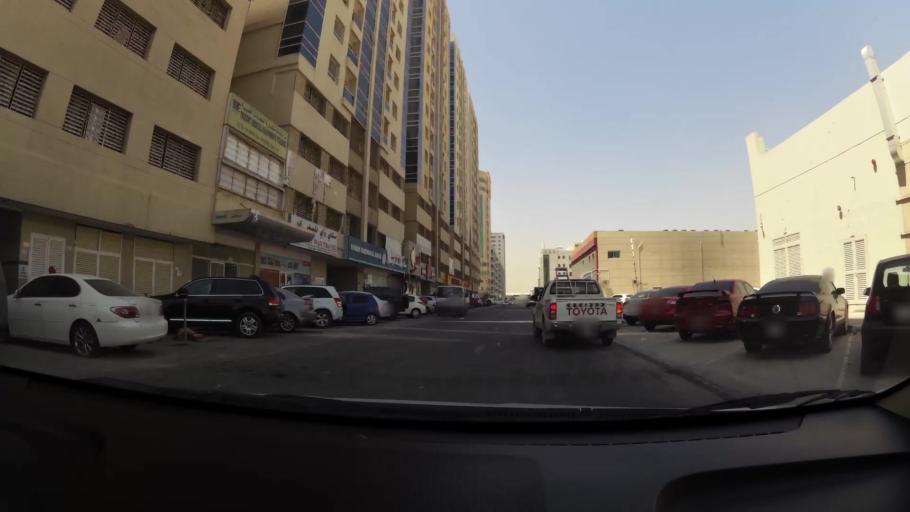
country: AE
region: Ajman
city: Ajman
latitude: 25.4057
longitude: 55.5080
